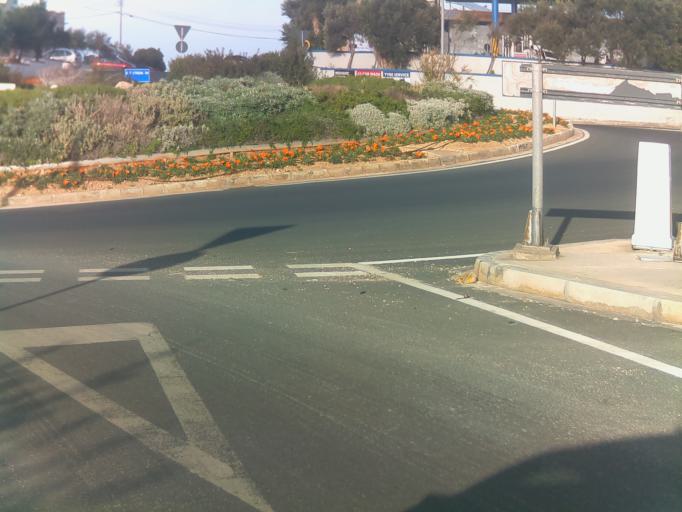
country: MT
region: Il-Mellieha
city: Mellieha
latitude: 35.9553
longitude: 14.3578
